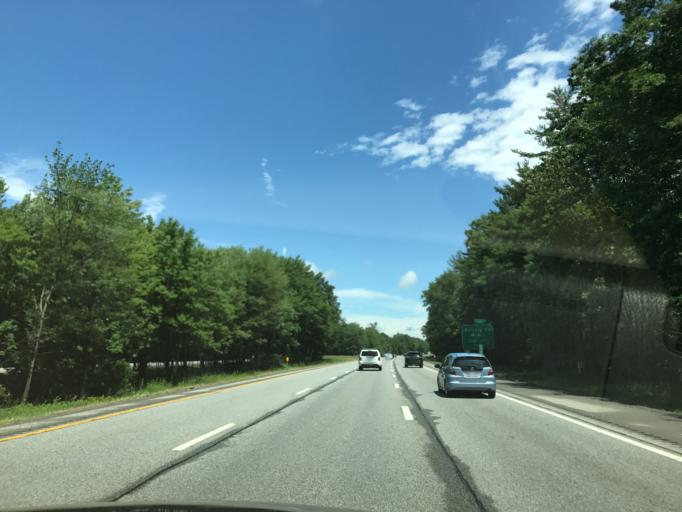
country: US
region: New York
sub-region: Saratoga County
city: Saratoga Springs
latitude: 43.1529
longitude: -73.7241
